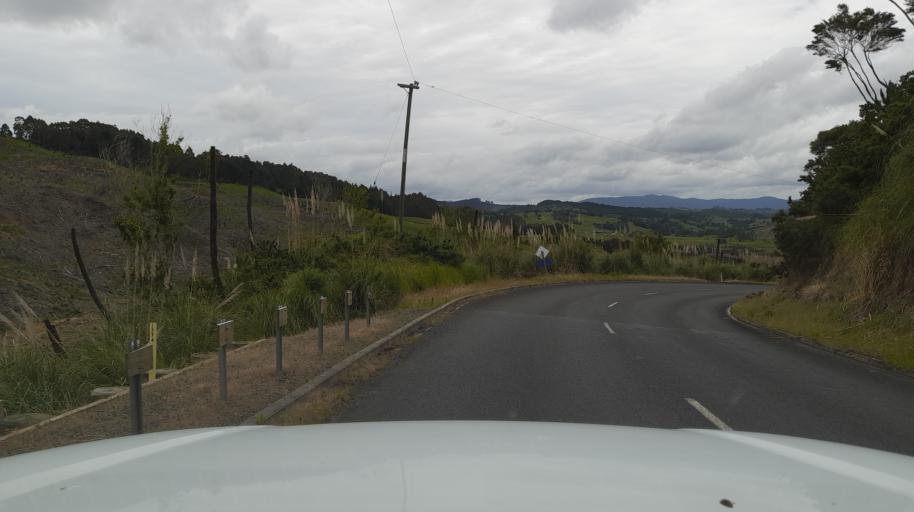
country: NZ
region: Northland
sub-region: Far North District
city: Kaitaia
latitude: -35.3693
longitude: 173.4318
